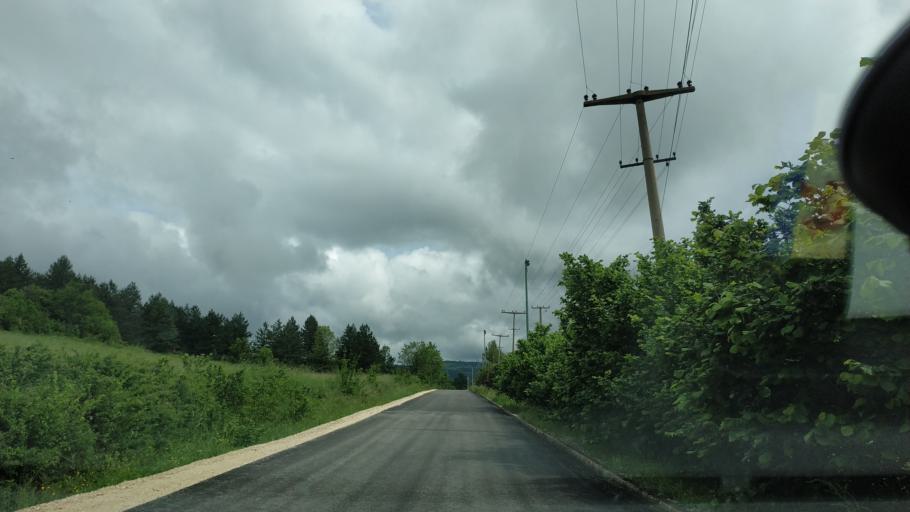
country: RS
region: Central Serbia
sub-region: Zajecarski Okrug
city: Soko Banja
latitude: 43.6484
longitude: 21.9002
